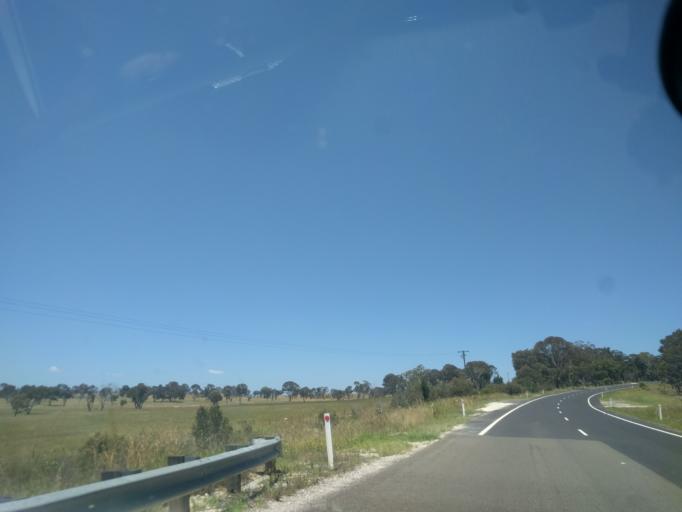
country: AU
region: New South Wales
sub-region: Armidale Dumaresq
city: Armidale
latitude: -30.5448
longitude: 151.7560
